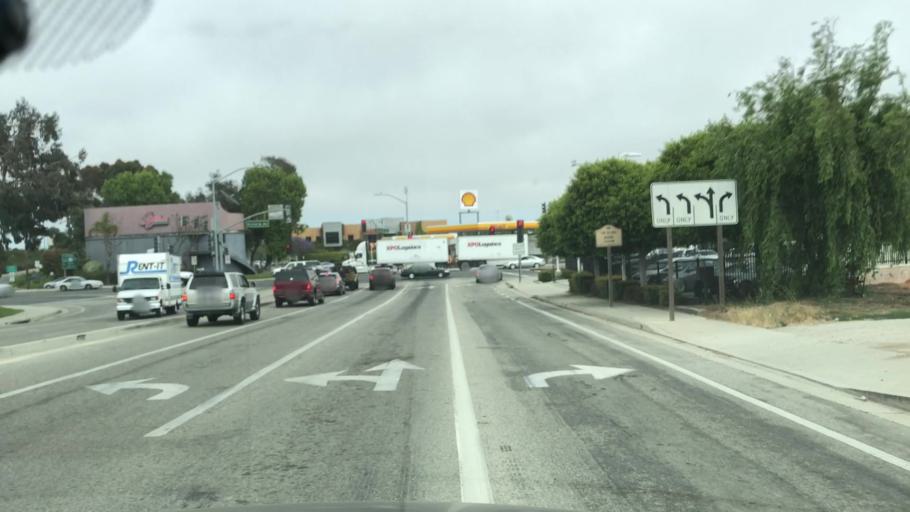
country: US
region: California
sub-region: Ventura County
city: El Rio
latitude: 34.2518
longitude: -119.2126
